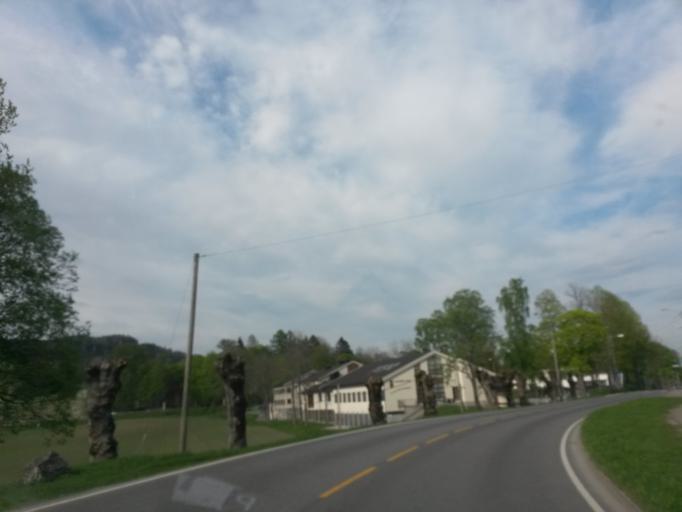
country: NO
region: Akershus
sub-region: Asker
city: Asker
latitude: 59.8477
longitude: 10.4410
